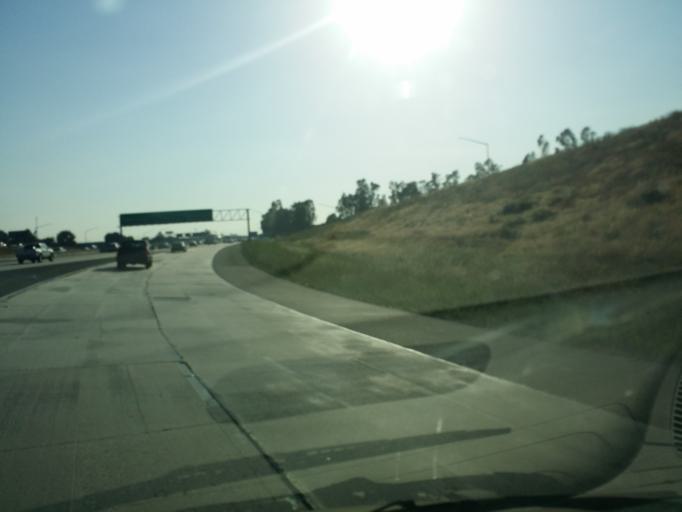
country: US
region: California
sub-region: San Bernardino County
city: Rancho Cucamonga
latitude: 34.0677
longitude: -117.5474
